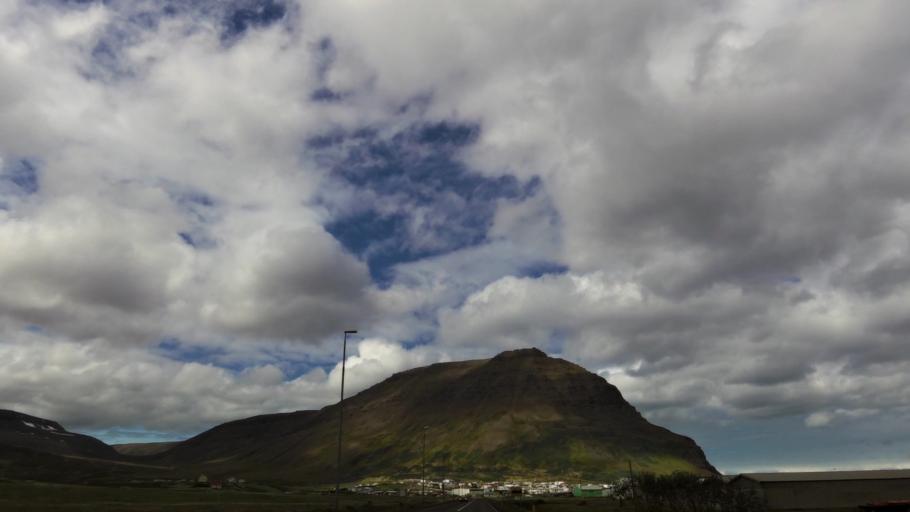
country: IS
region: Westfjords
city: Isafjoerdur
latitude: 66.1500
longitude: -23.2446
